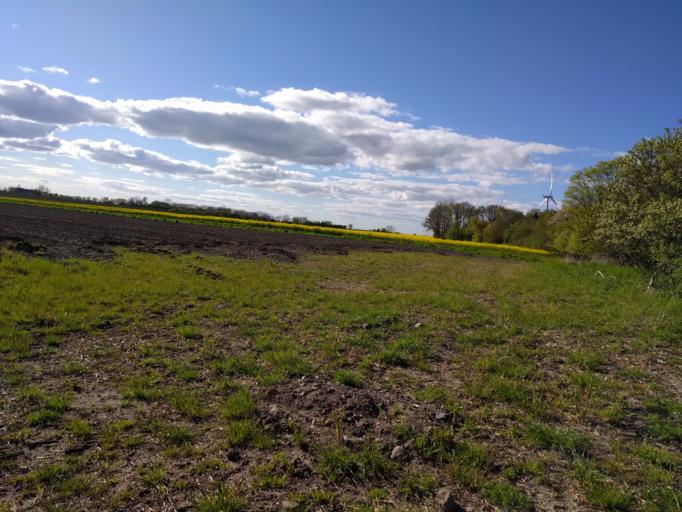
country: DK
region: South Denmark
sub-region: Kerteminde Kommune
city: Munkebo
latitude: 55.4577
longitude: 10.5120
